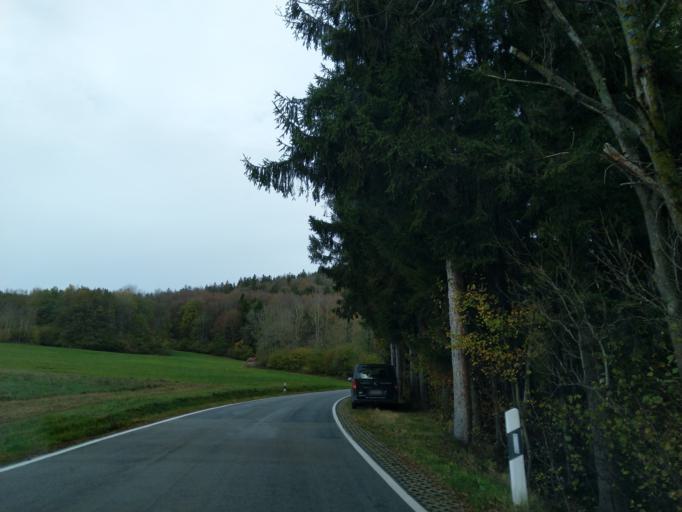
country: DE
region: Bavaria
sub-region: Lower Bavaria
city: Schofweg
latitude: 48.8045
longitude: 13.2259
